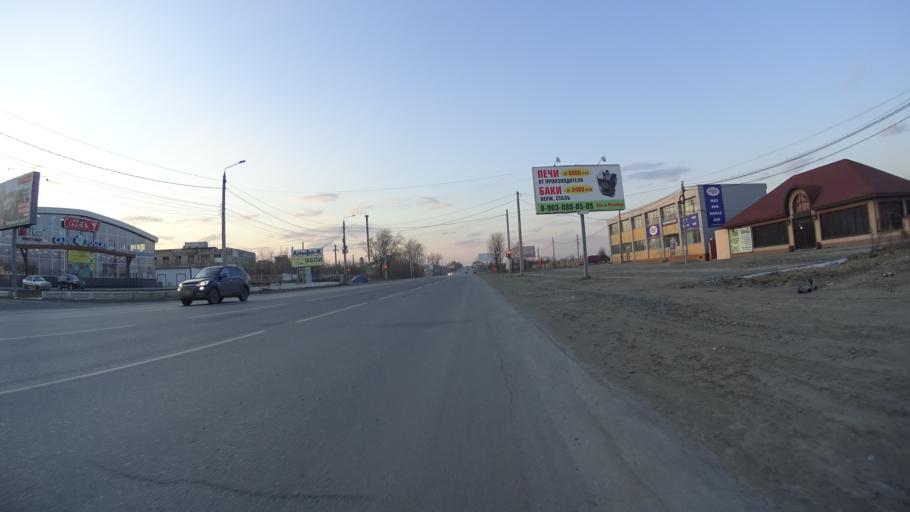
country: RU
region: Chelyabinsk
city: Novosineglazovskiy
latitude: 55.0942
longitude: 61.3882
